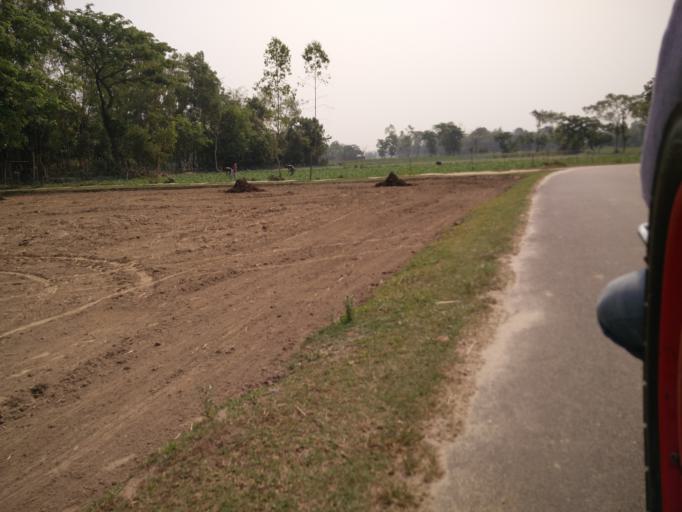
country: BD
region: Dhaka
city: Muktagacha
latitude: 24.8903
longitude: 90.2692
